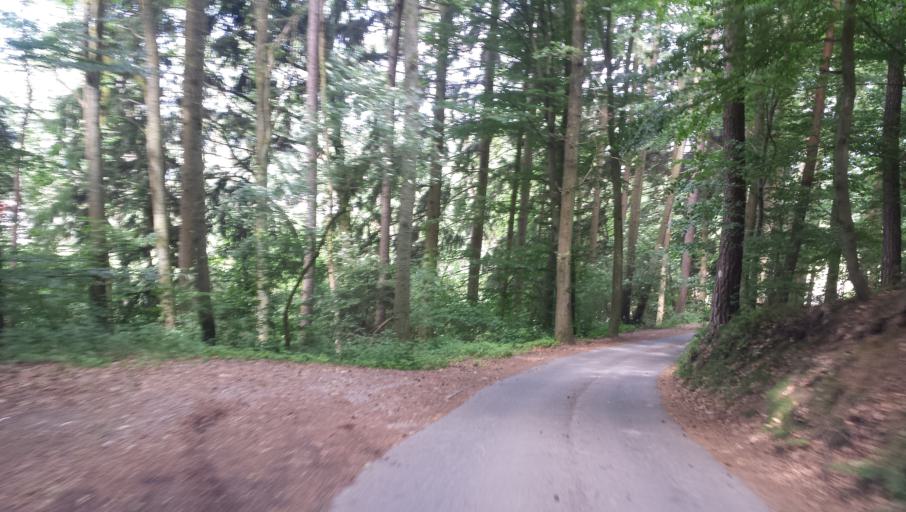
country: DE
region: Hesse
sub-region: Regierungsbezirk Darmstadt
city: Wald-Michelbach
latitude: 49.6139
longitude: 8.8369
